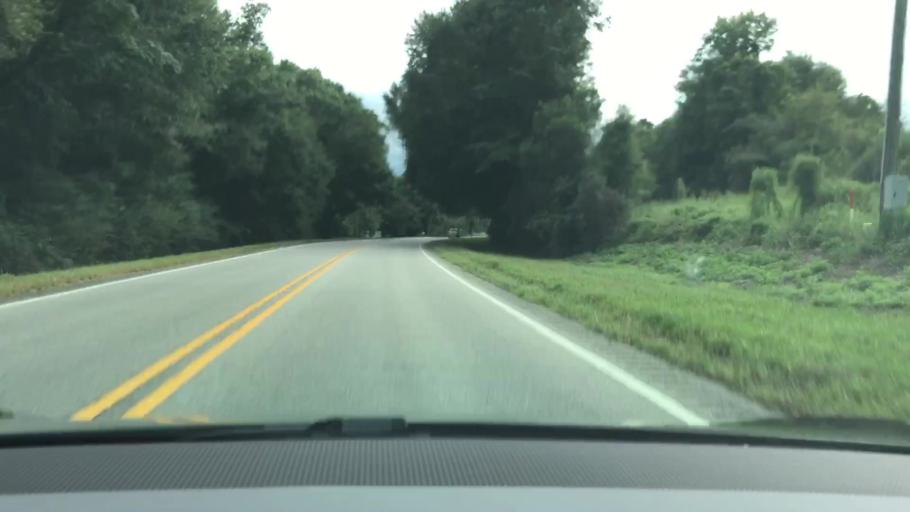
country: US
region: Alabama
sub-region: Coffee County
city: Elba
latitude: 31.5332
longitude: -86.0302
